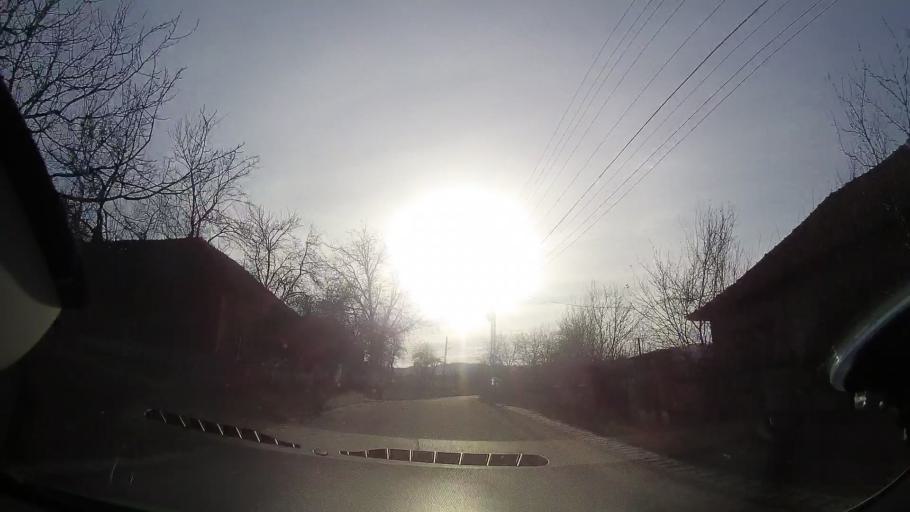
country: RO
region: Bihor
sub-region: Comuna Sarbi
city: Burzuc
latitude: 47.1422
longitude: 22.1847
